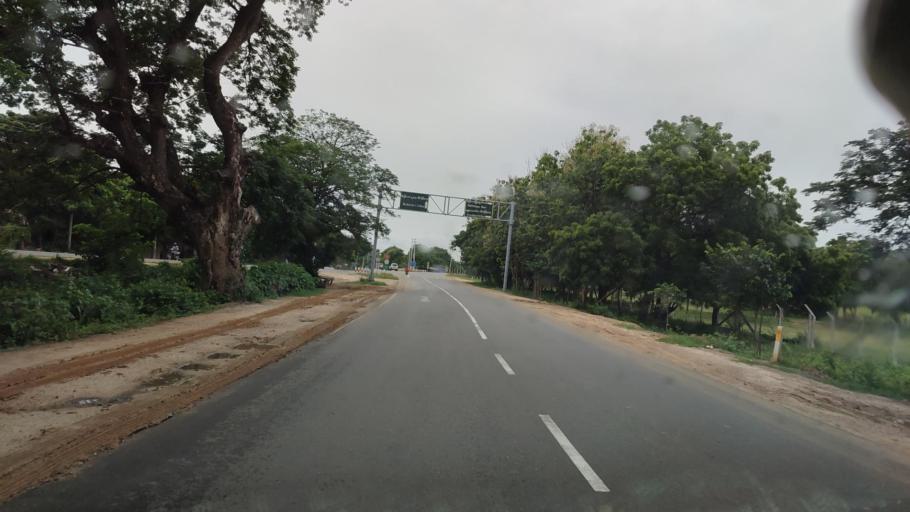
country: MM
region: Mandalay
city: Meiktila
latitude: 20.7937
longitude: 95.9111
